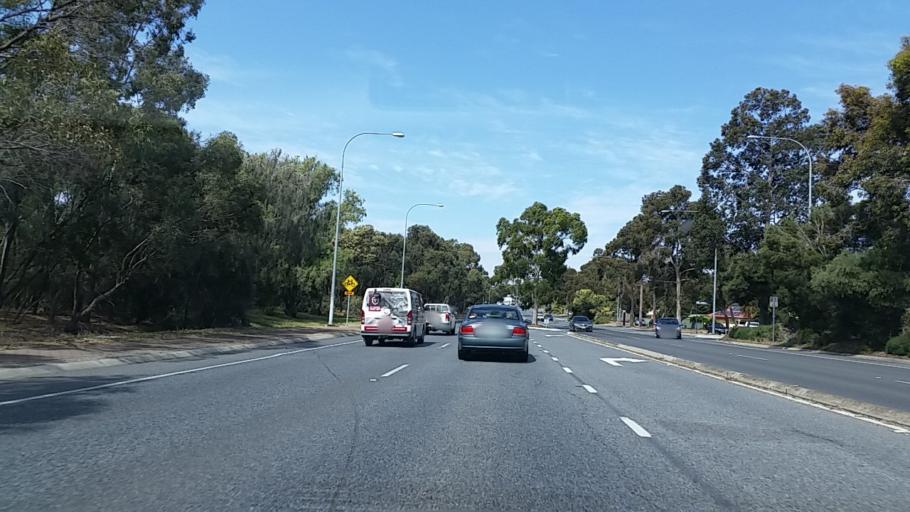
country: AU
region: South Australia
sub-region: Salisbury
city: Ingle Farm
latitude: -34.8243
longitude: 138.6293
